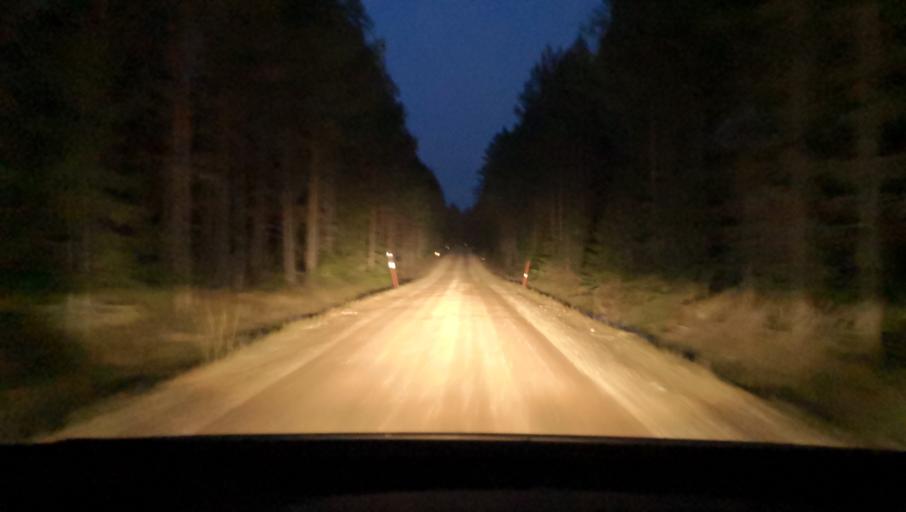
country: SE
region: OErebro
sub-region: Lindesbergs Kommun
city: Frovi
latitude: 59.6422
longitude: 15.4800
